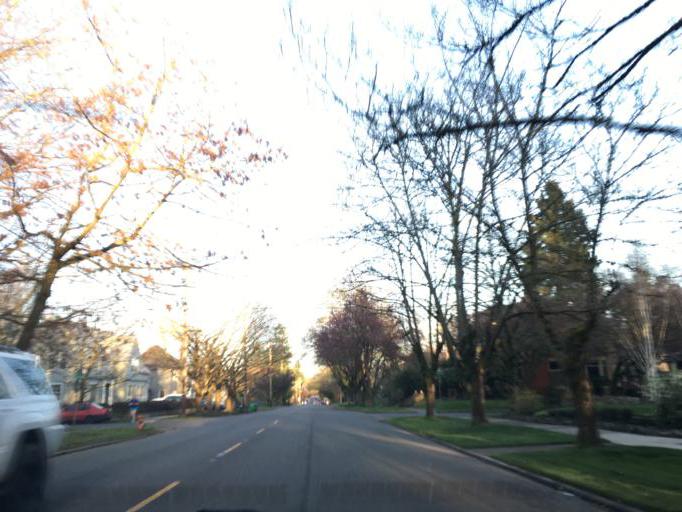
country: US
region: Oregon
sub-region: Multnomah County
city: Portland
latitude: 45.5421
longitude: -122.6480
